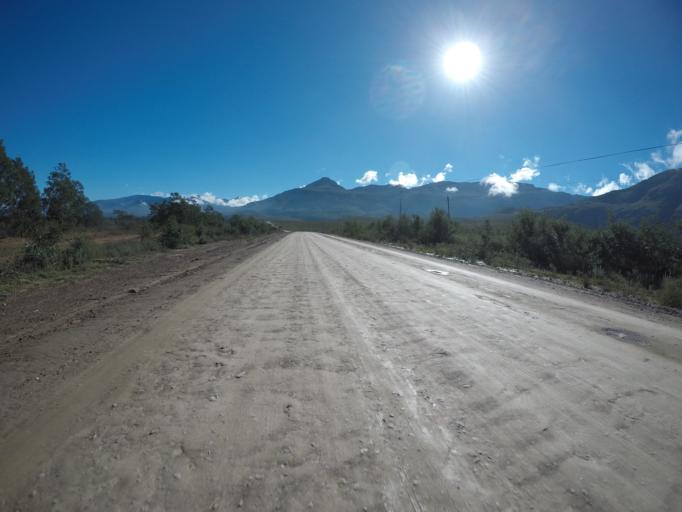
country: ZA
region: Western Cape
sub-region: Overberg District Municipality
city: Caledon
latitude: -34.0665
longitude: 19.6290
